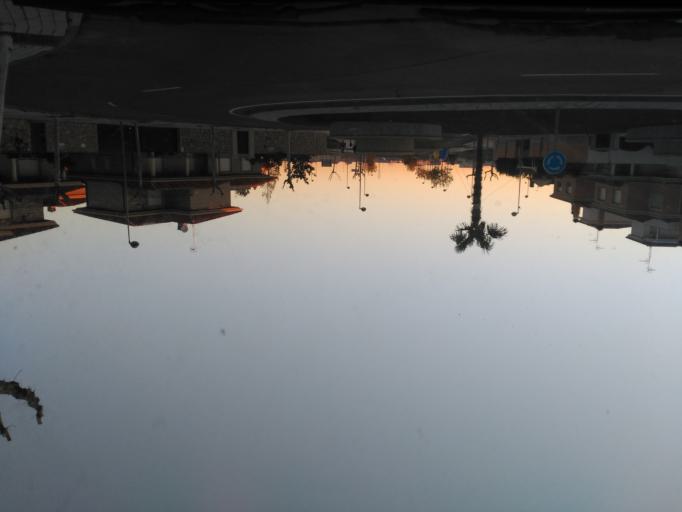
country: ES
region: Castille and Leon
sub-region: Provincia de Salamanca
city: Carbajosa de la Sagrada
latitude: 40.9404
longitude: -5.6449
